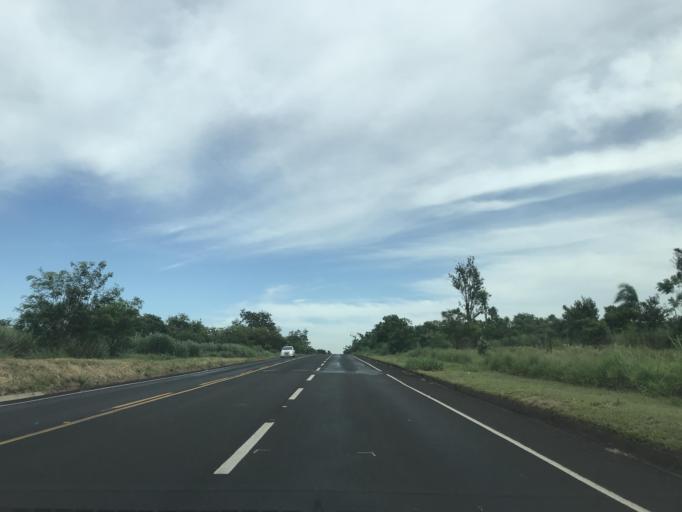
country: BR
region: Parana
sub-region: Paranavai
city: Nova Aurora
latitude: -22.9977
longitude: -52.5750
